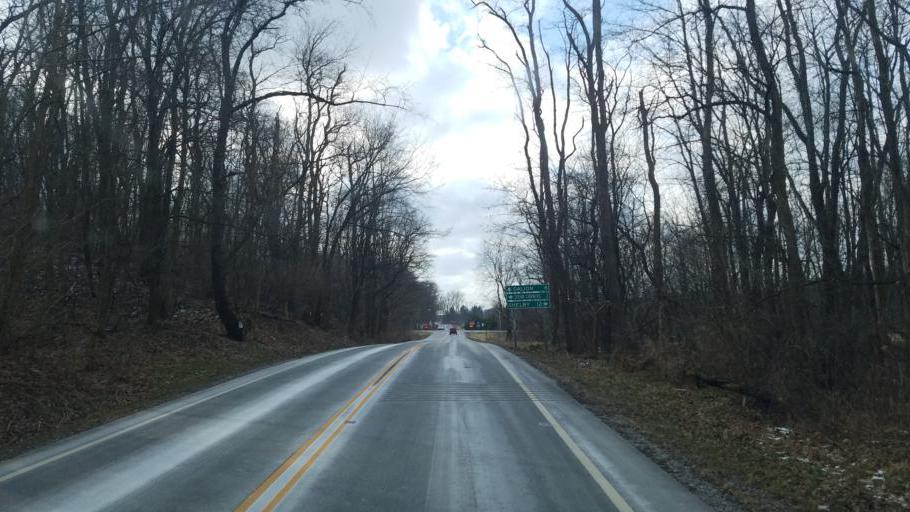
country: US
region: Ohio
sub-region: Richland County
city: Lexington
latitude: 40.7056
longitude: -82.6629
